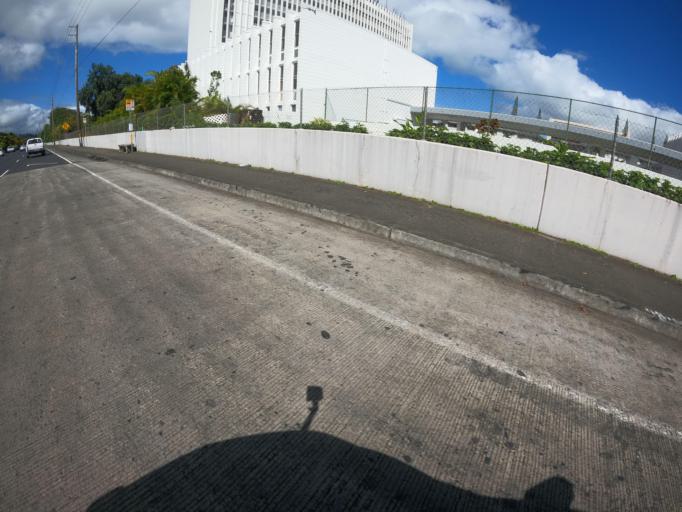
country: US
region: Hawaii
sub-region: Honolulu County
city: Kane'ohe
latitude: 21.4137
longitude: -157.8106
